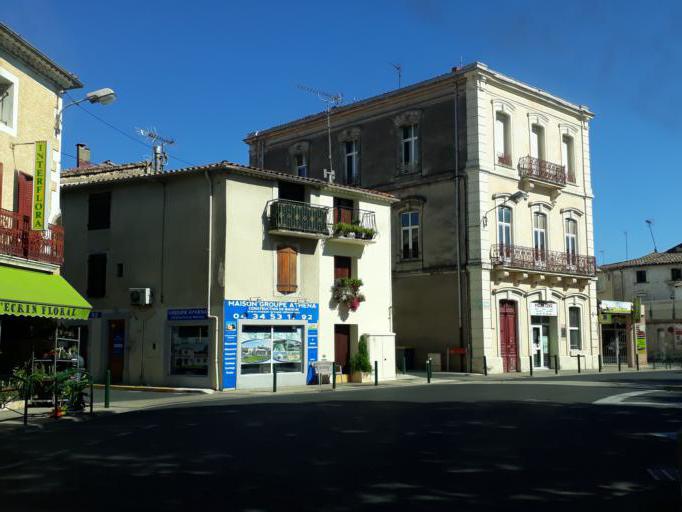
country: FR
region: Languedoc-Roussillon
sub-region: Departement de l'Herault
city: Florensac
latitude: 43.3827
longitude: 3.4664
